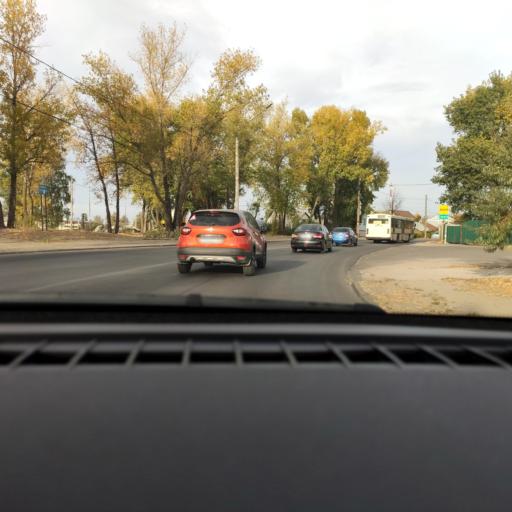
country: RU
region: Voronezj
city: Voronezh
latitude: 51.7319
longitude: 39.2602
